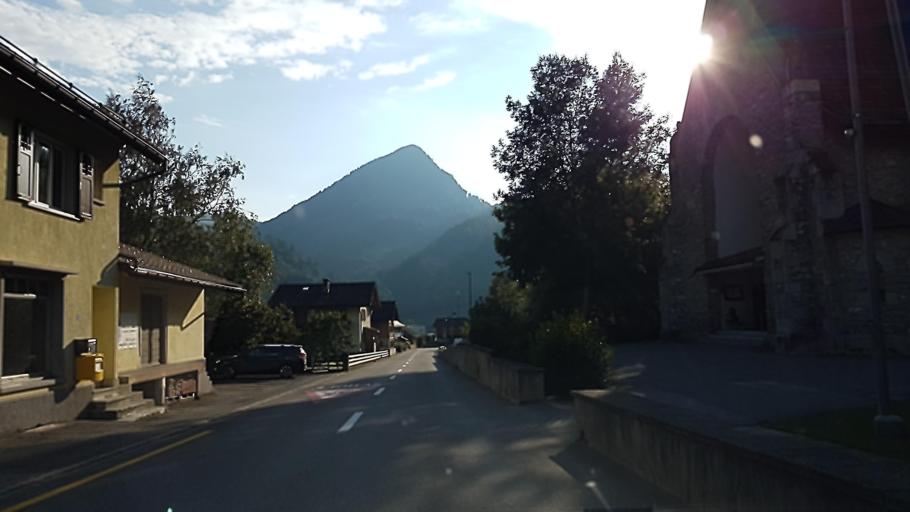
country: CH
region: Grisons
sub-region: Praettigau/Davos District
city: Grusch
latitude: 46.9793
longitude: 9.6389
